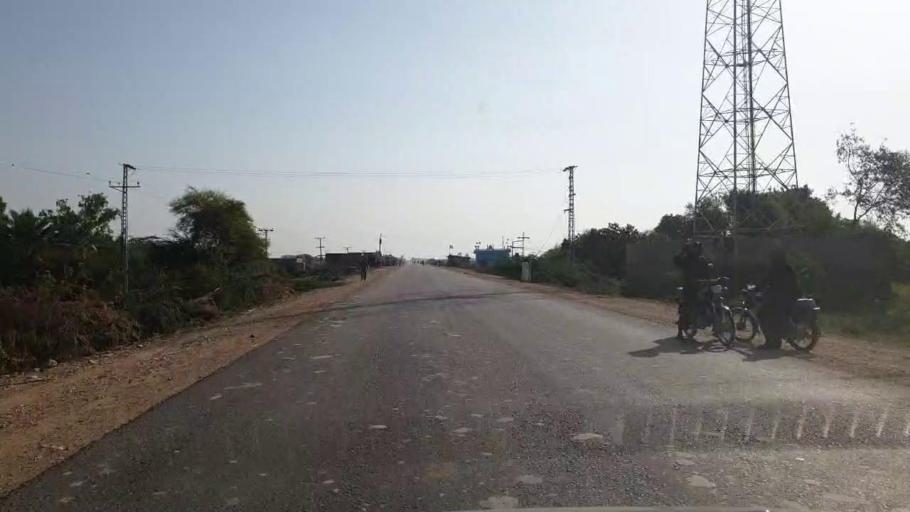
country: PK
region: Sindh
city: Badin
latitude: 24.6584
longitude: 68.9538
